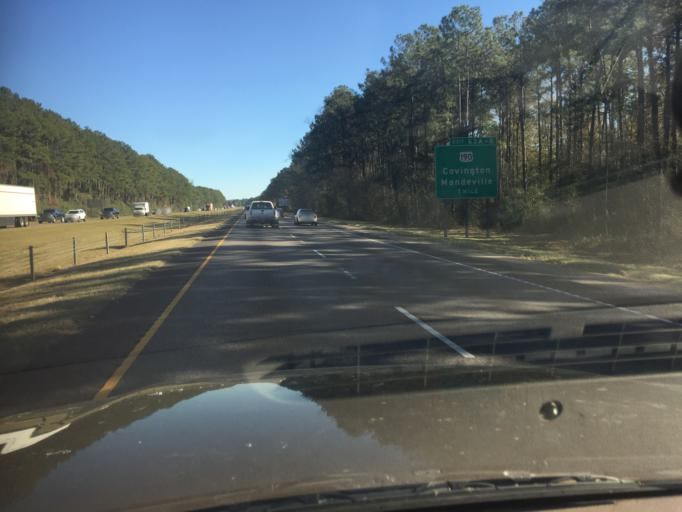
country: US
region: Louisiana
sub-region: Saint Tammany Parish
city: Covington
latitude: 30.4360
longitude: -90.1084
